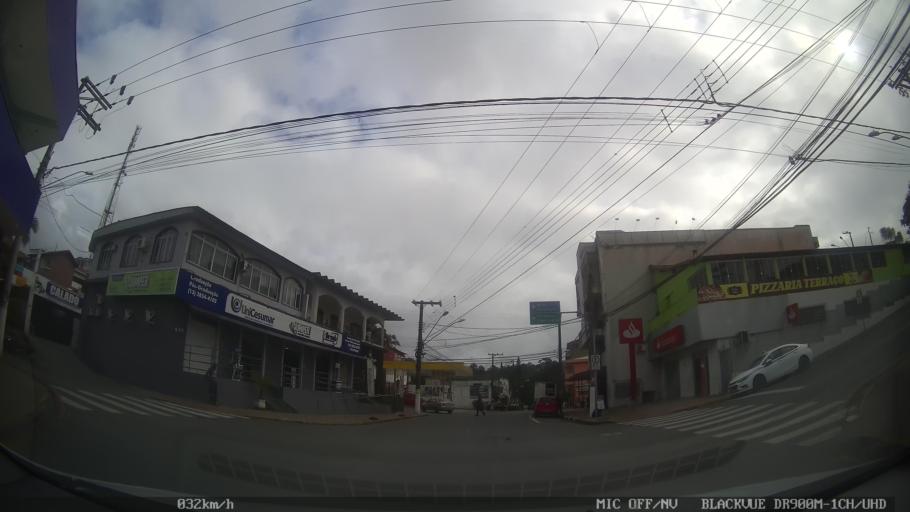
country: BR
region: Sao Paulo
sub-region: Cajati
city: Cajati
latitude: -24.7267
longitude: -48.1121
